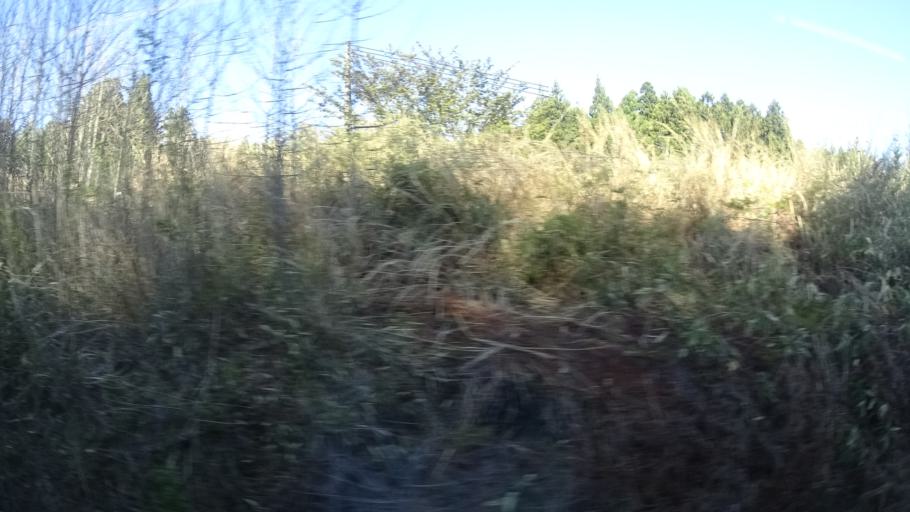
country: JP
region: Fukushima
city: Namie
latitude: 37.5871
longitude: 141.0019
